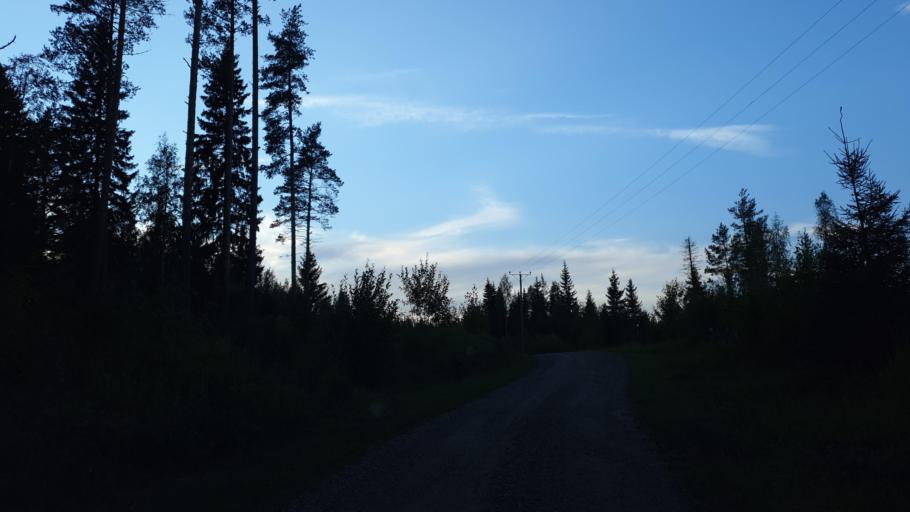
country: FI
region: Northern Savo
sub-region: Koillis-Savo
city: Kaavi
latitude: 62.9791
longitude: 28.7795
